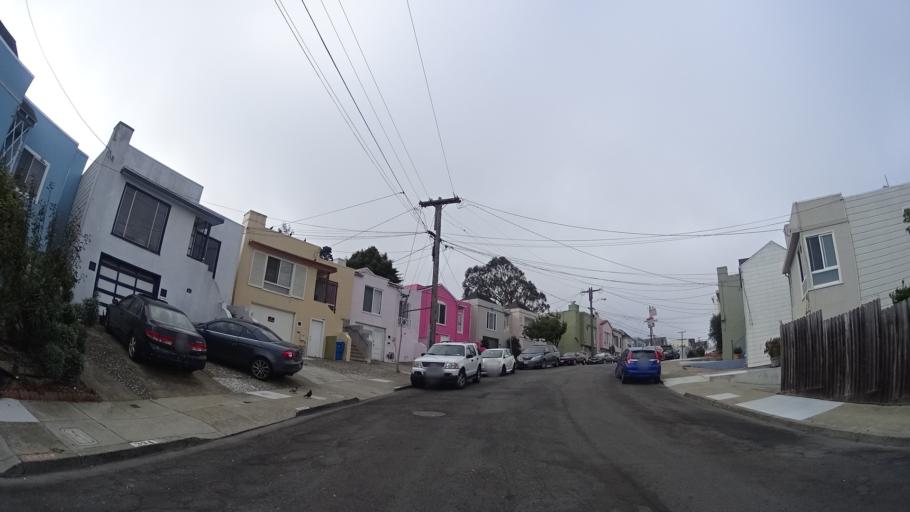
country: US
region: California
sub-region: San Francisco County
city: San Francisco
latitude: 37.7304
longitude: -122.4235
